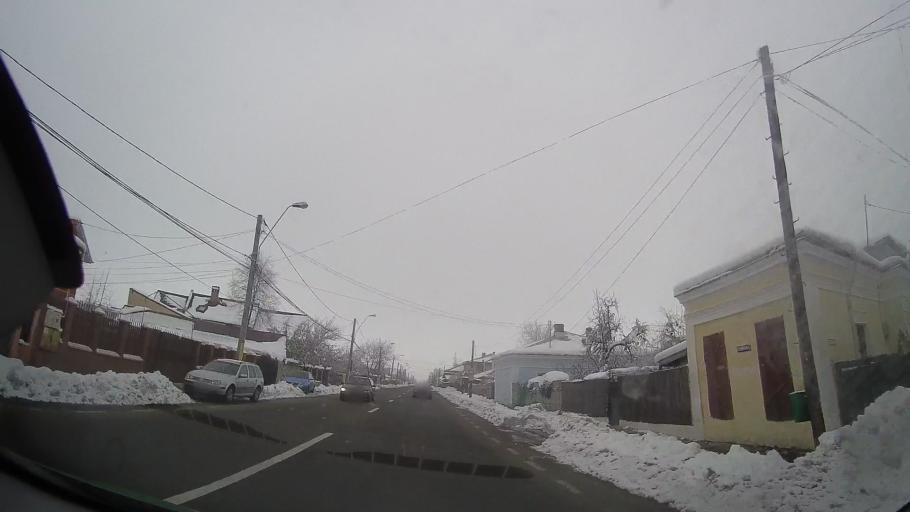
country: RO
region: Neamt
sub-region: Municipiul Roman
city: Roman
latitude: 46.9319
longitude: 26.9401
